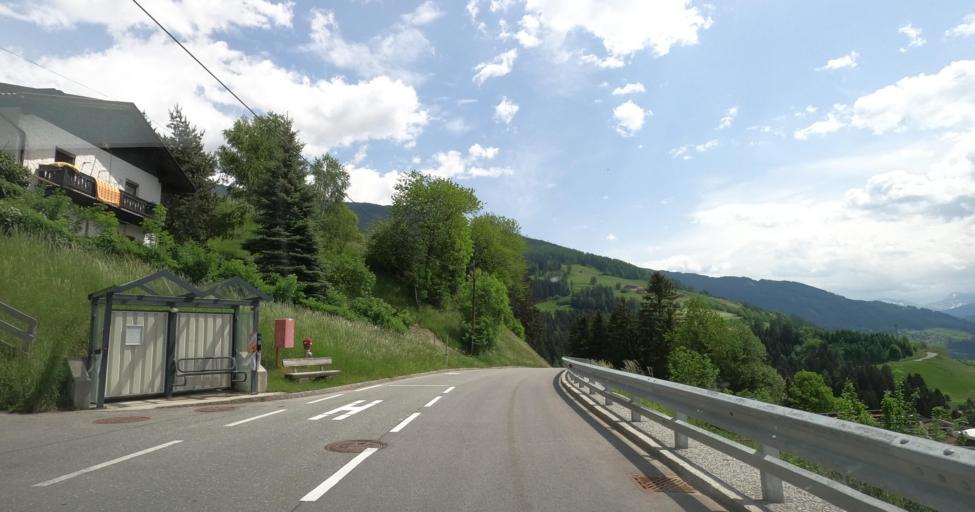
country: AT
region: Tyrol
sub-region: Politischer Bezirk Innsbruck Land
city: Ellbogen
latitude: 47.1647
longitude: 11.4506
